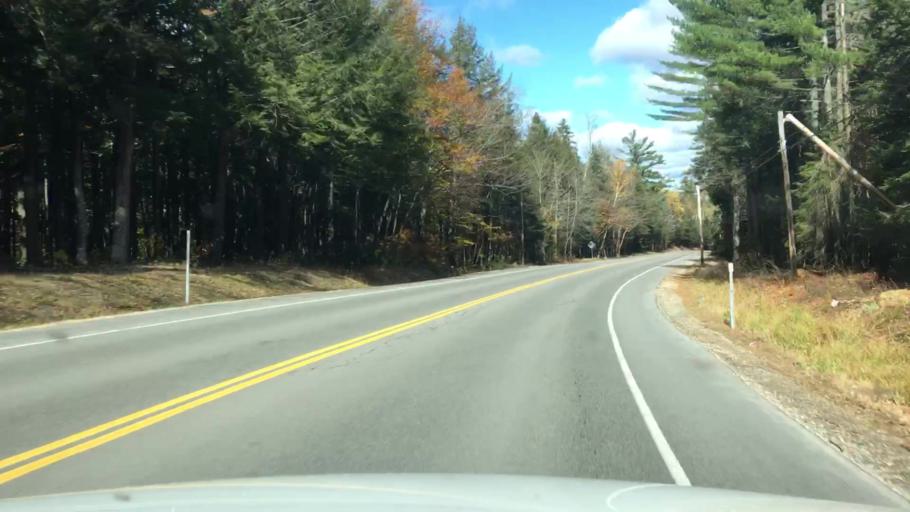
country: US
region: New Hampshire
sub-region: Coos County
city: Gorham
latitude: 44.3481
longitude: -71.1955
